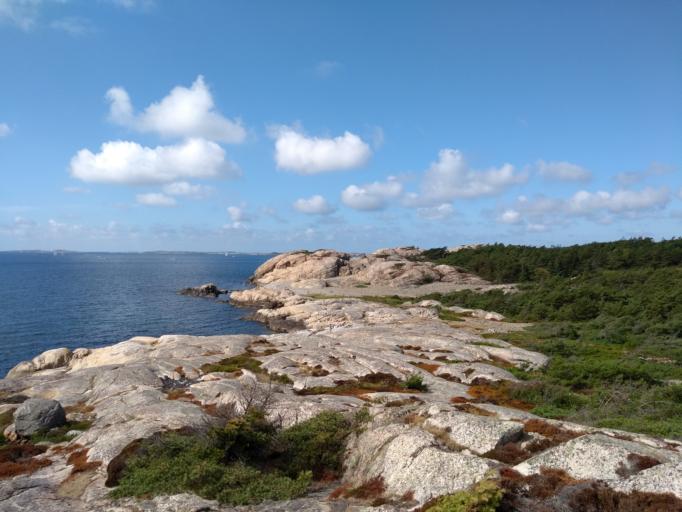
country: SE
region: Vaestra Goetaland
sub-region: Stromstads Kommun
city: Stroemstad
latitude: 58.8654
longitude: 11.1300
